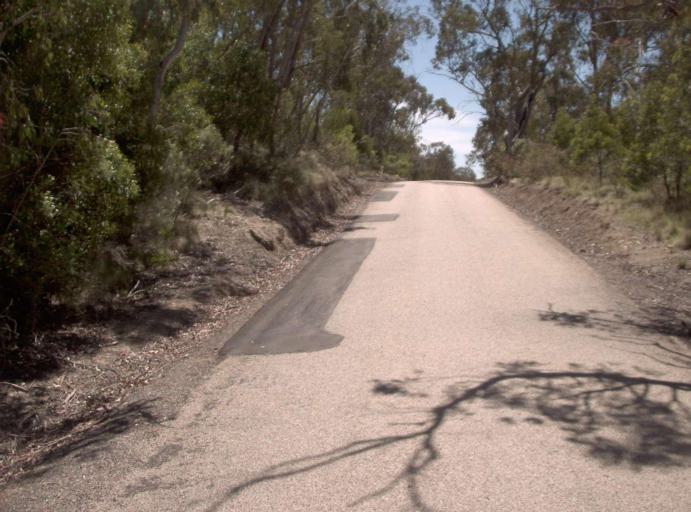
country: AU
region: Victoria
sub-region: East Gippsland
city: Lakes Entrance
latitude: -37.1268
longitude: 148.2453
